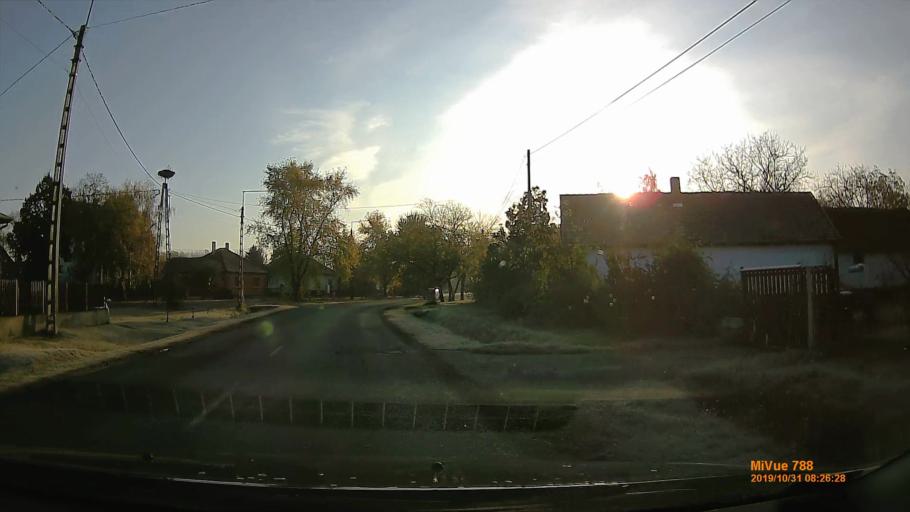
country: HU
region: Pest
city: Tapiobicske
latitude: 47.3652
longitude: 19.6785
